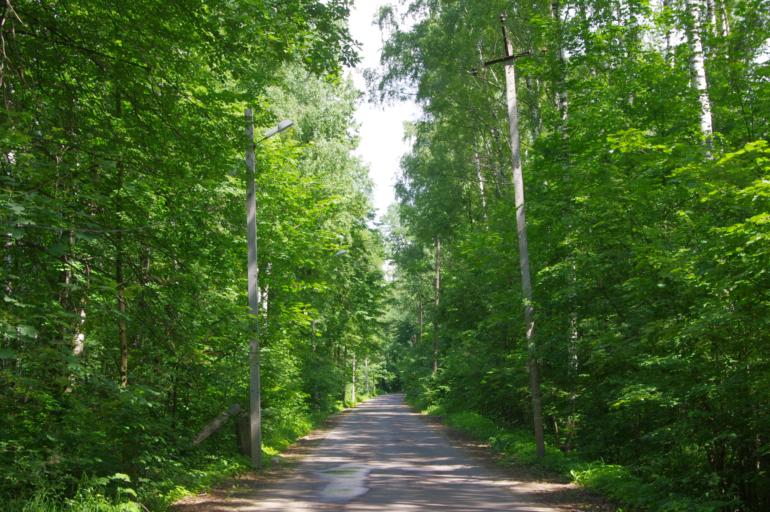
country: RU
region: Moskovskaya
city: Malyshevo
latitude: 55.5487
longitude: 38.3031
